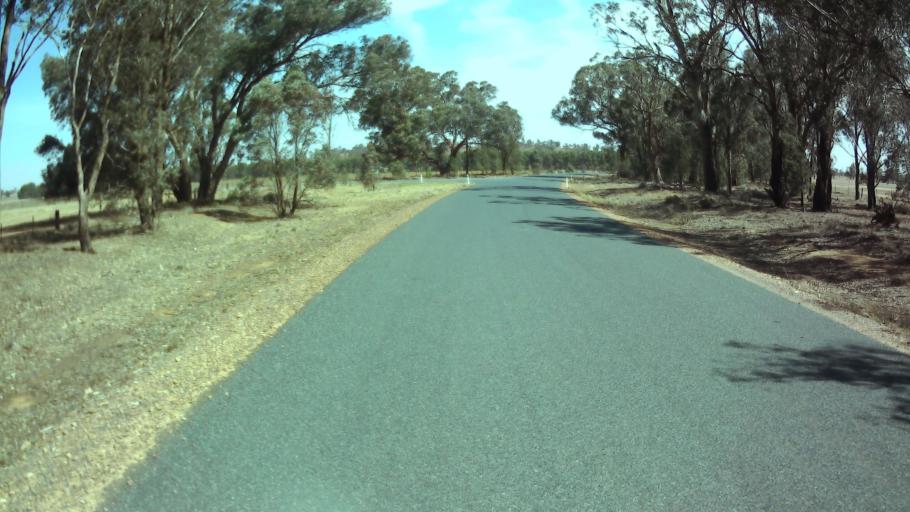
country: AU
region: New South Wales
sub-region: Weddin
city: Grenfell
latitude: -34.0372
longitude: 148.1346
